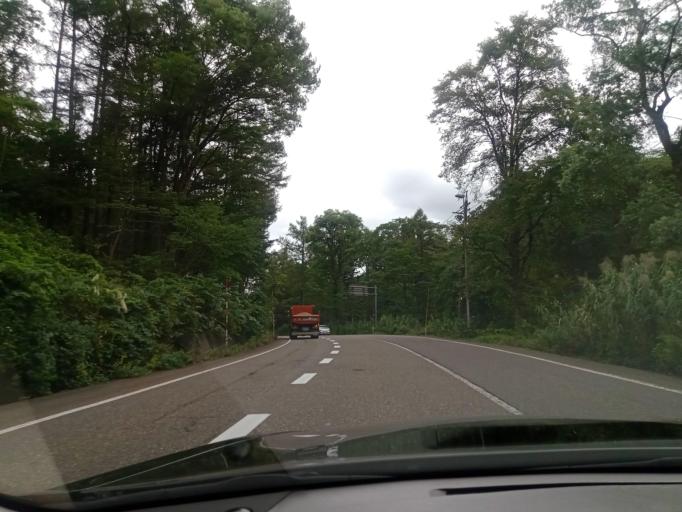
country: JP
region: Niigata
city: Arai
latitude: 36.8457
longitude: 138.1989
